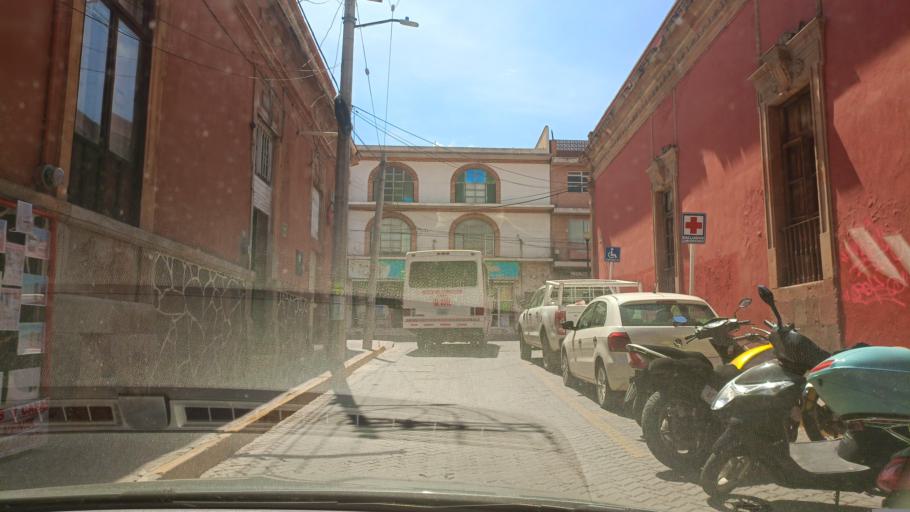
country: MX
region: Guerrero
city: San Luis de la Paz
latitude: 21.2975
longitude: -100.5154
